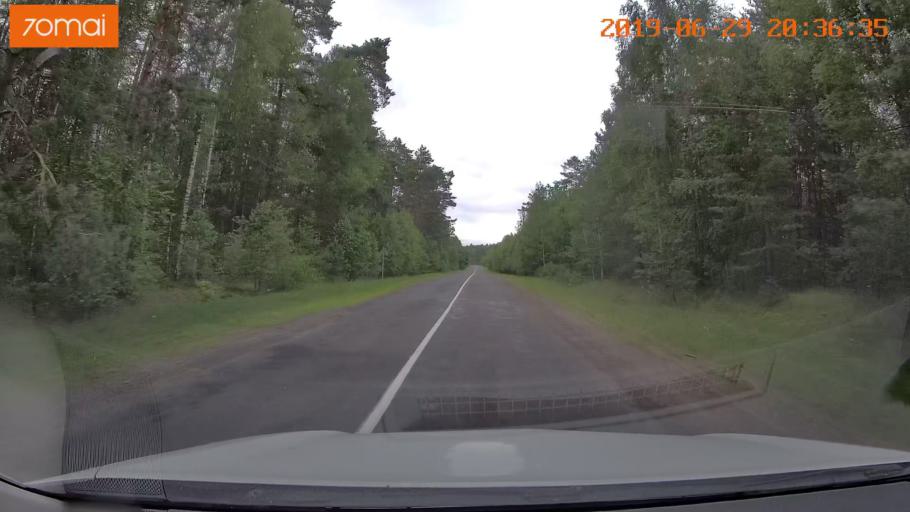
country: BY
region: Brest
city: Hantsavichy
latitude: 52.5279
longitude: 26.3597
